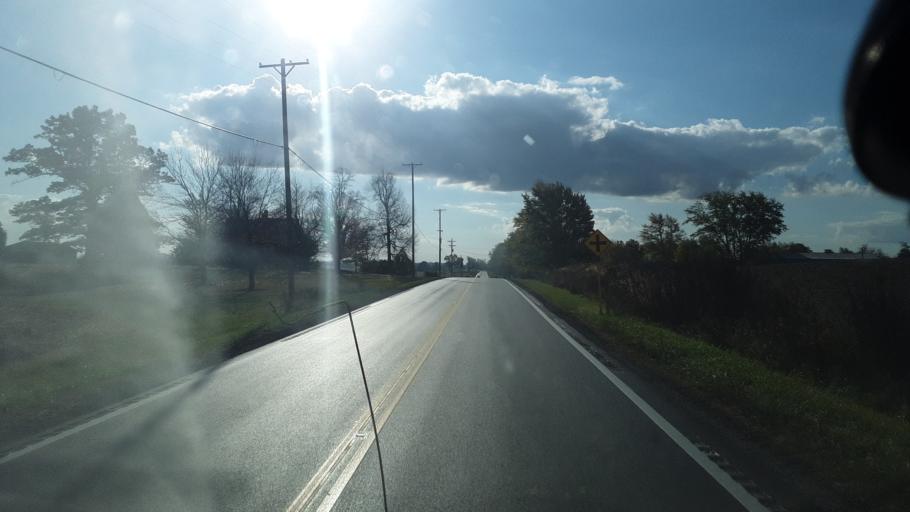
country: US
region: Ohio
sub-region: Fayette County
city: Jeffersonville
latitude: 39.5963
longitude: -83.5147
